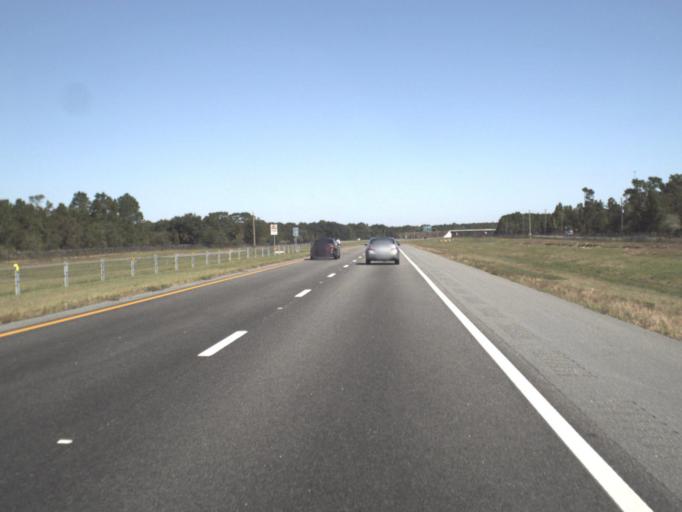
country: US
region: Florida
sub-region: Pasco County
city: Shady Hills
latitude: 28.3763
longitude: -82.5416
